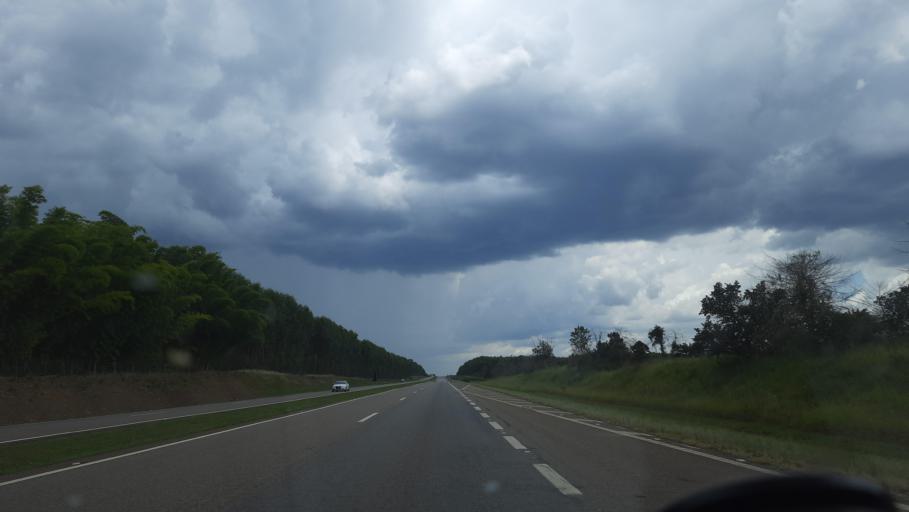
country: BR
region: Sao Paulo
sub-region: Casa Branca
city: Casa Branca
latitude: -21.8599
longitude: -47.0626
